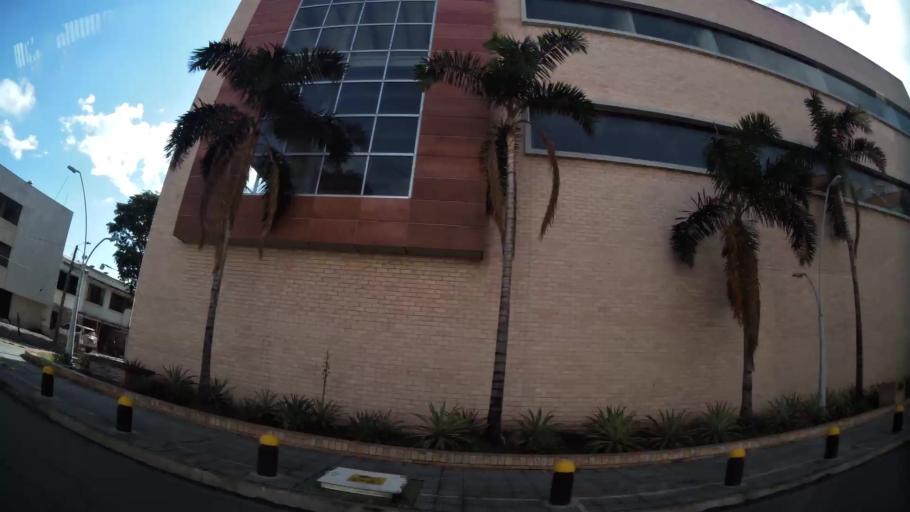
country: CO
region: Valle del Cauca
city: Cali
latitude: 3.4273
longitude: -76.5379
